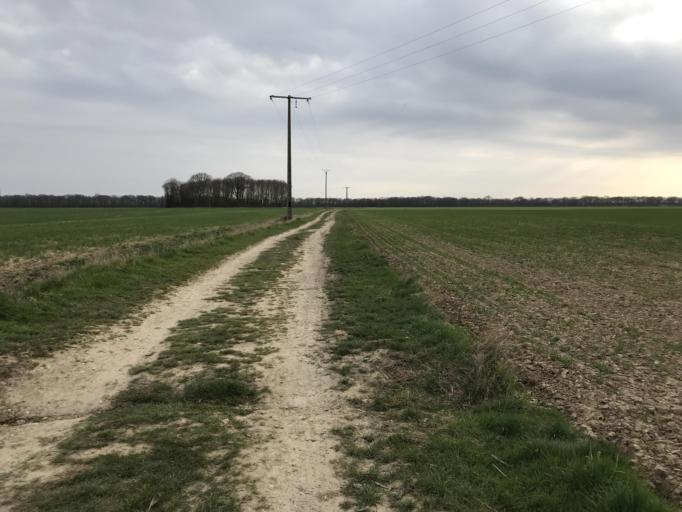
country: FR
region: Ile-de-France
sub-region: Departement de l'Essonne
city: Les Molieres
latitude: 48.6592
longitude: 2.0539
